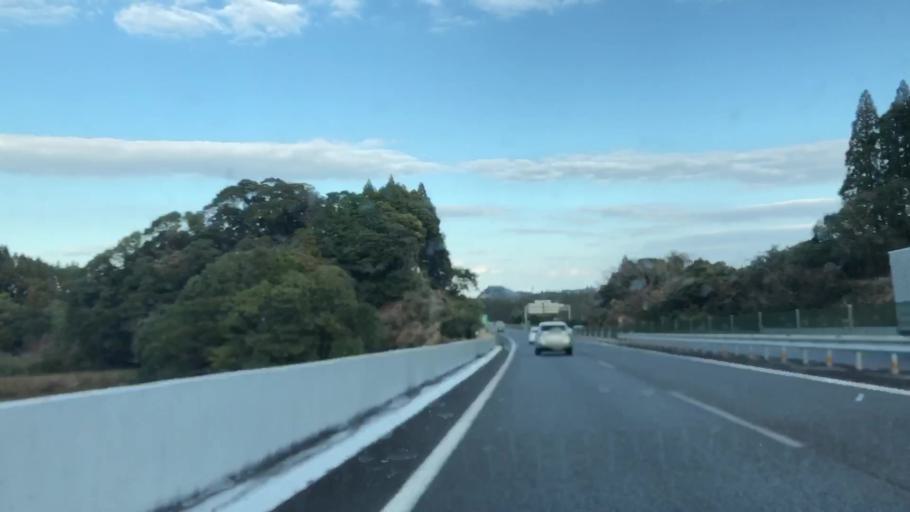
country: JP
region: Miyazaki
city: Miyazaki-shi
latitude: 31.8531
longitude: 131.3697
